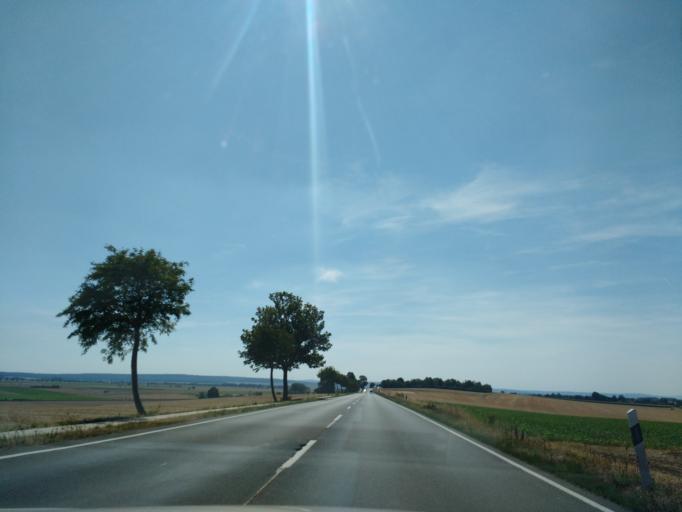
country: DE
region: Lower Saxony
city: Sohlde
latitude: 52.2056
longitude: 10.1686
